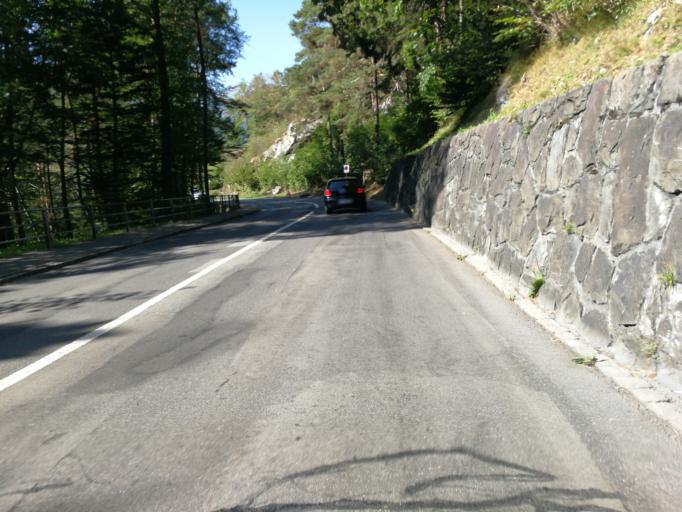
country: CH
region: Schwyz
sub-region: Bezirk Gersau
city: Gersau
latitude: 46.9925
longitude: 8.5580
